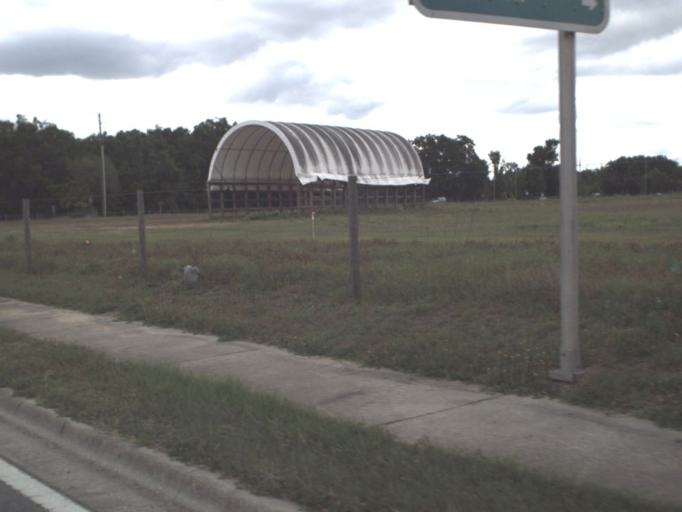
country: US
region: Florida
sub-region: Marion County
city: Ocala
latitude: 29.2670
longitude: -82.1795
